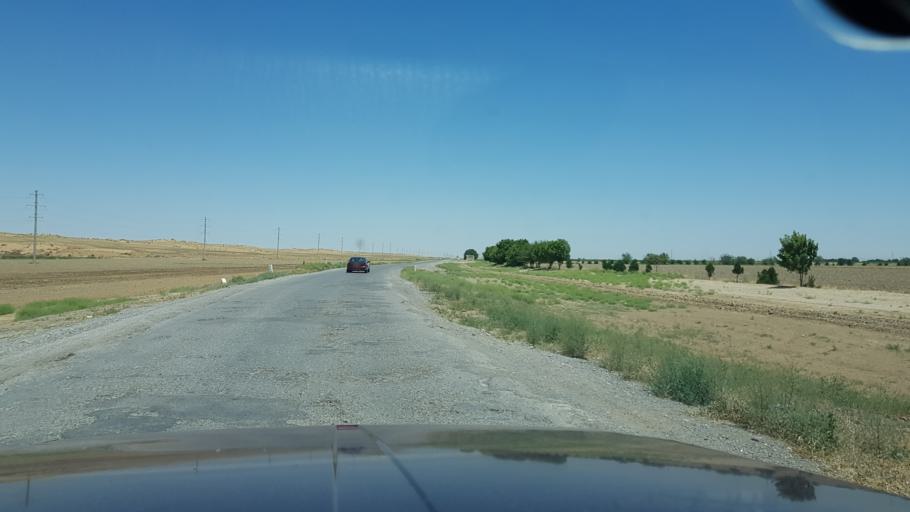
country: TM
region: Ahal
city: Annau
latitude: 37.8586
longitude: 58.7079
